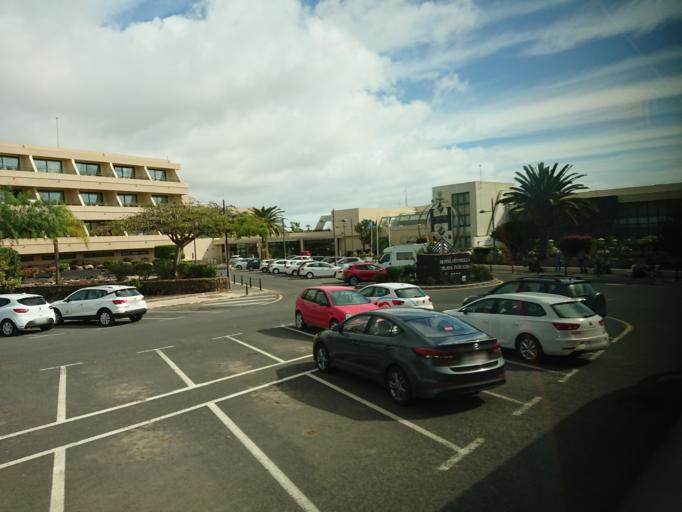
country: ES
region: Canary Islands
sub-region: Provincia de Las Palmas
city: Playa Blanca
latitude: 28.8635
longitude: -13.8215
